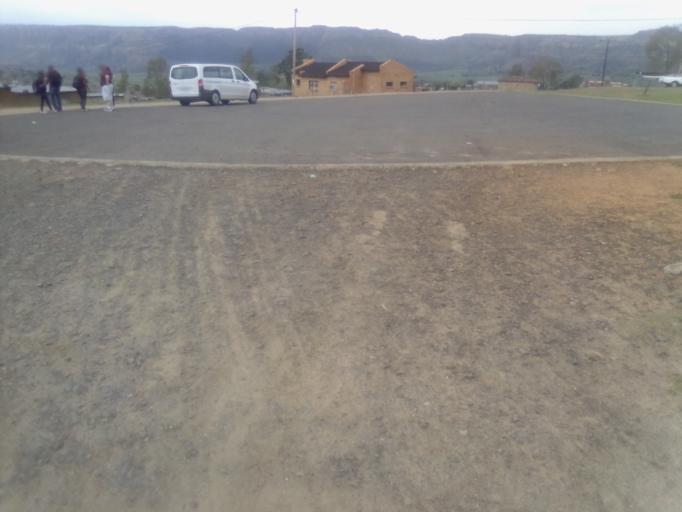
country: LS
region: Leribe
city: Leribe
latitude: -29.0328
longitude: 28.0256
